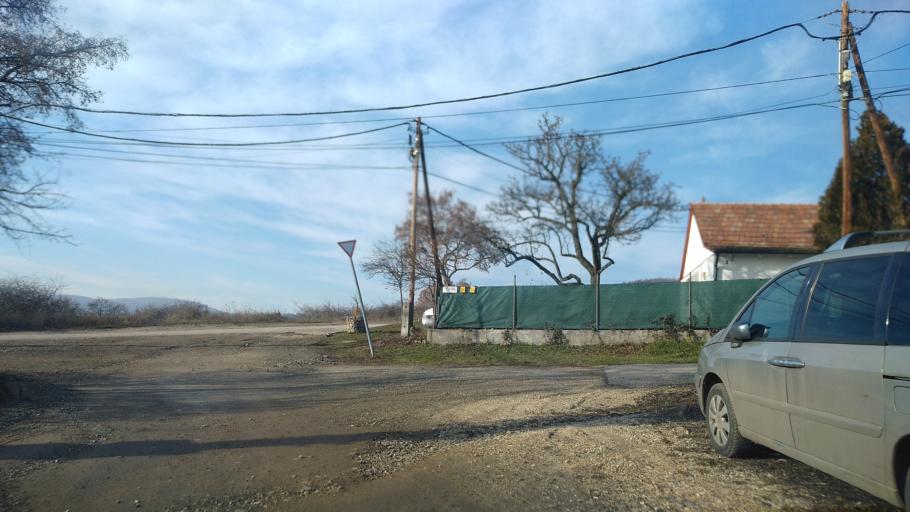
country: HU
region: Pest
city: Leanyfalu
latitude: 47.7003
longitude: 19.0514
